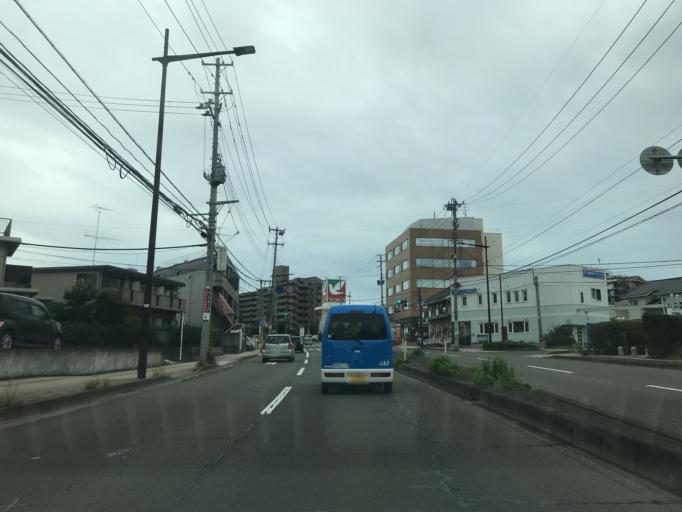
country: JP
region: Miyagi
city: Sendai-shi
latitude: 38.3120
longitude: 140.8871
